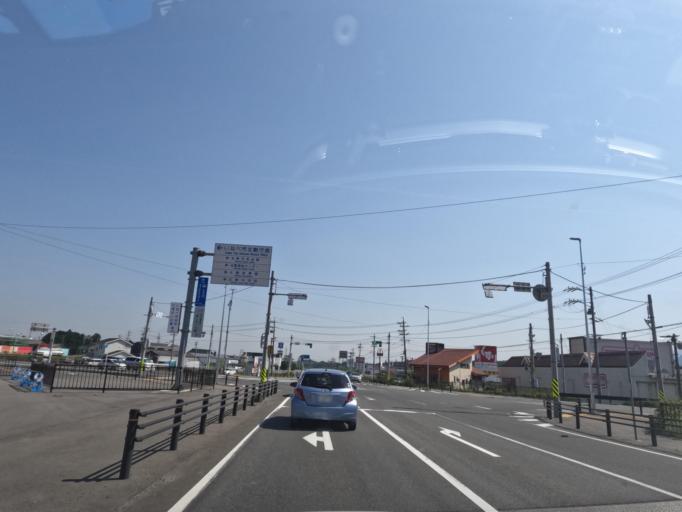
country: JP
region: Mie
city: Komono
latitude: 35.1561
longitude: 136.5100
